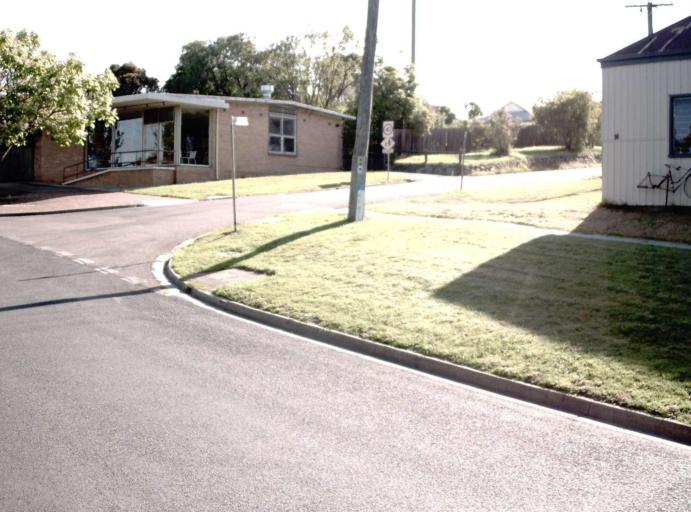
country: AU
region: Victoria
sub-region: East Gippsland
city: Lakes Entrance
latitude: -37.7089
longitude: 148.4540
